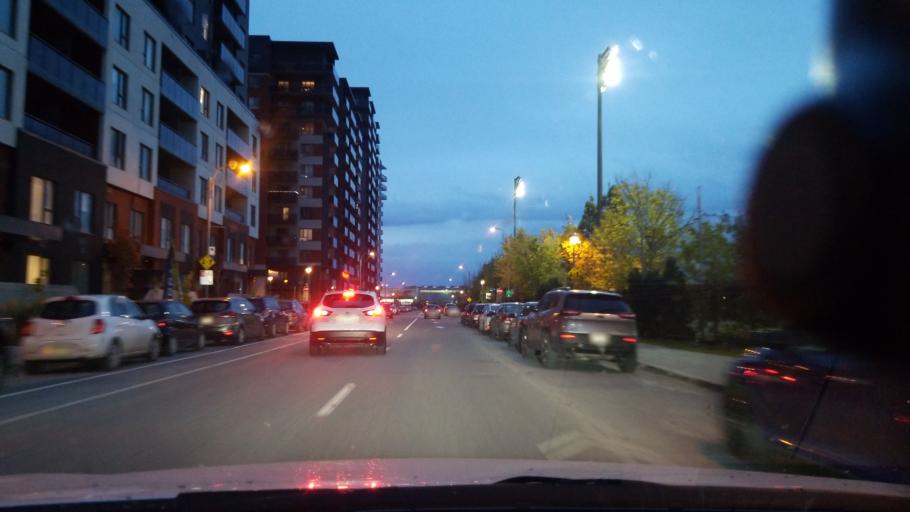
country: CA
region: Quebec
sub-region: Laval
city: Laval
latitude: 45.5592
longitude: -73.7232
